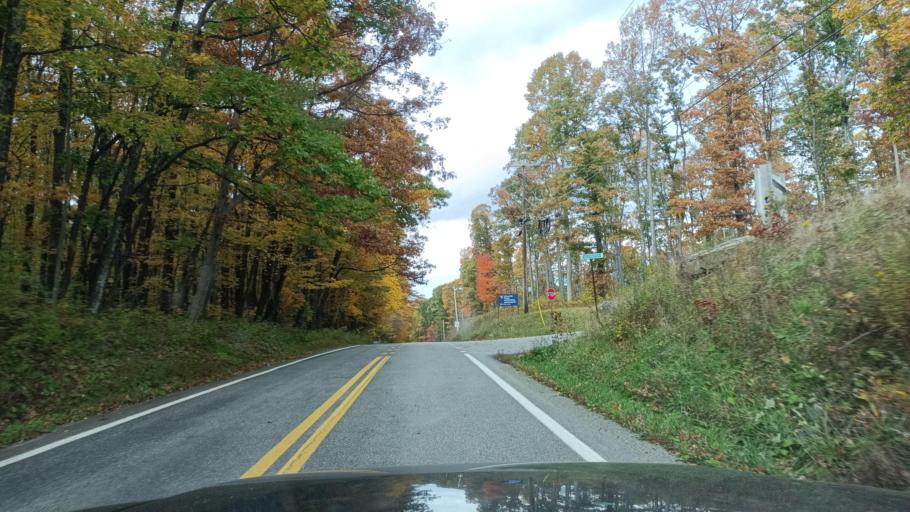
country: US
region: West Virginia
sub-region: Monongalia County
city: Cheat Lake
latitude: 39.6591
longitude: -79.7709
